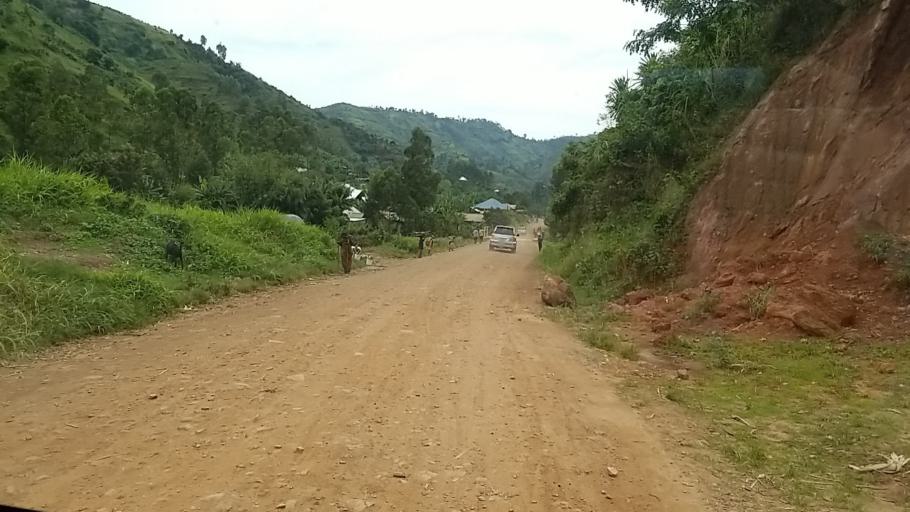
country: CD
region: Nord Kivu
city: Sake
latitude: -1.7257
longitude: 29.0105
